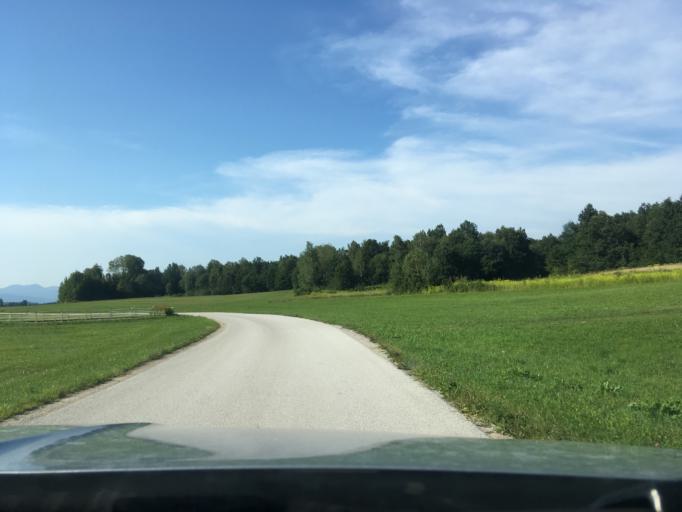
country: SI
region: Crnomelj
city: Crnomelj
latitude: 45.4578
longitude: 15.2165
